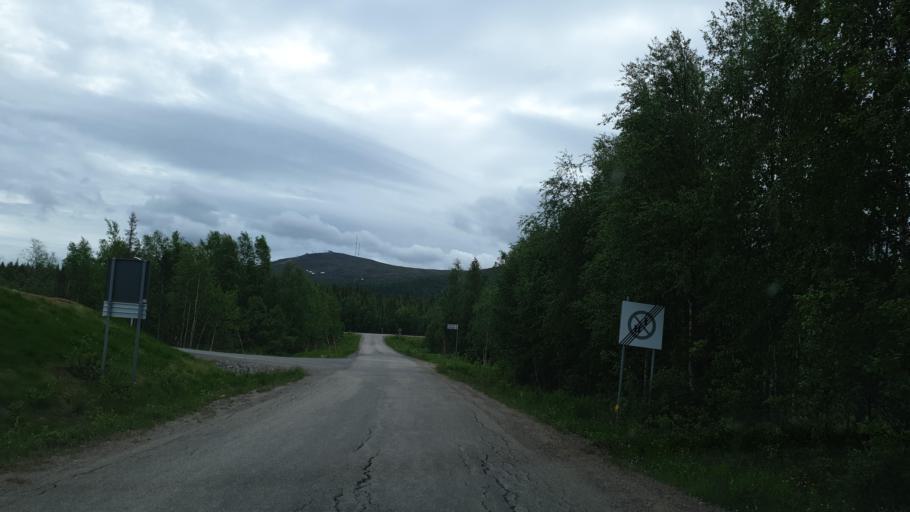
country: SE
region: Norrbotten
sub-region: Gallivare Kommun
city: Gaellivare
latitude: 67.1308
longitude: 20.6264
